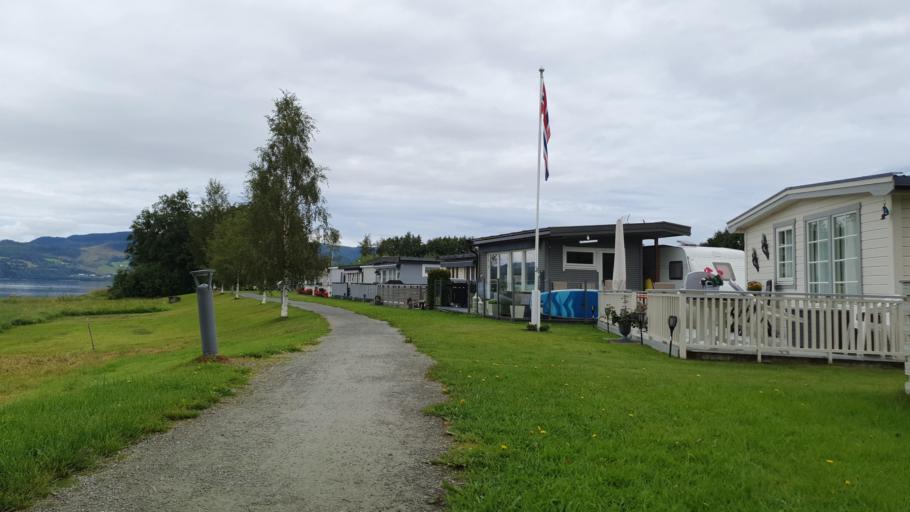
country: NO
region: Sor-Trondelag
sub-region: Selbu
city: Mebonden
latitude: 63.2291
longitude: 11.0235
